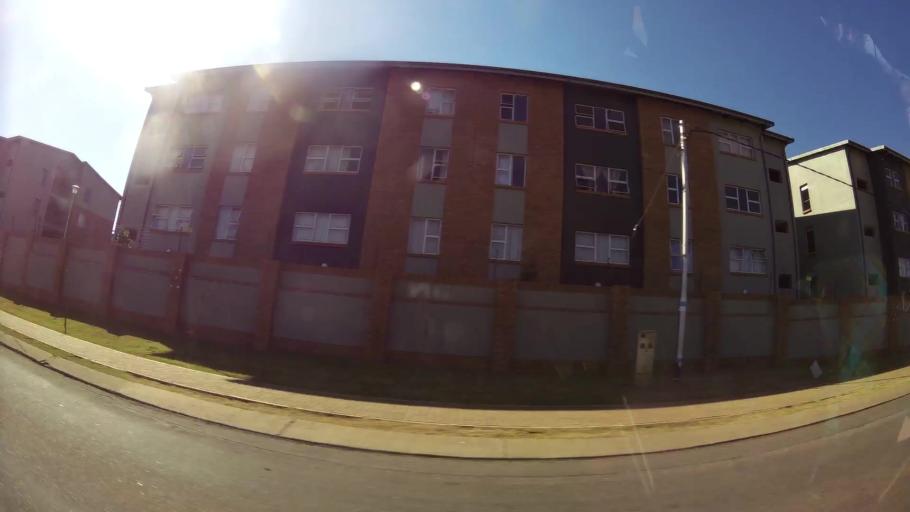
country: ZA
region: Gauteng
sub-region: City of Tshwane Metropolitan Municipality
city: Centurion
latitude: -25.8529
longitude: 28.2019
